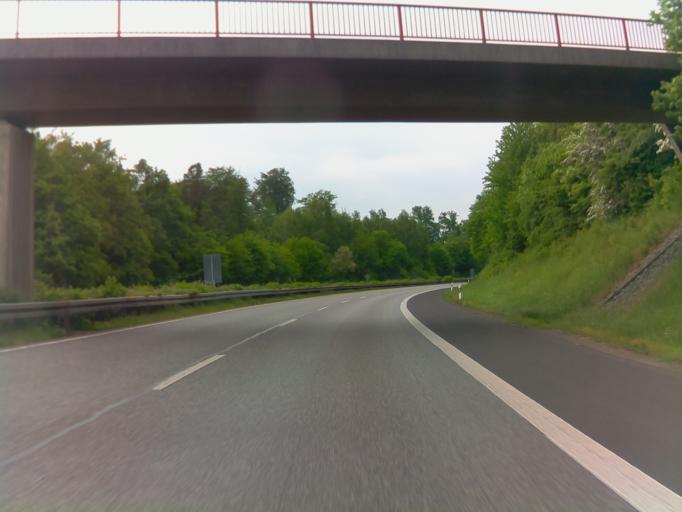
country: DE
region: Hesse
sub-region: Regierungsbezirk Giessen
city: Fronhausen
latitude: 50.7081
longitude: 8.7271
